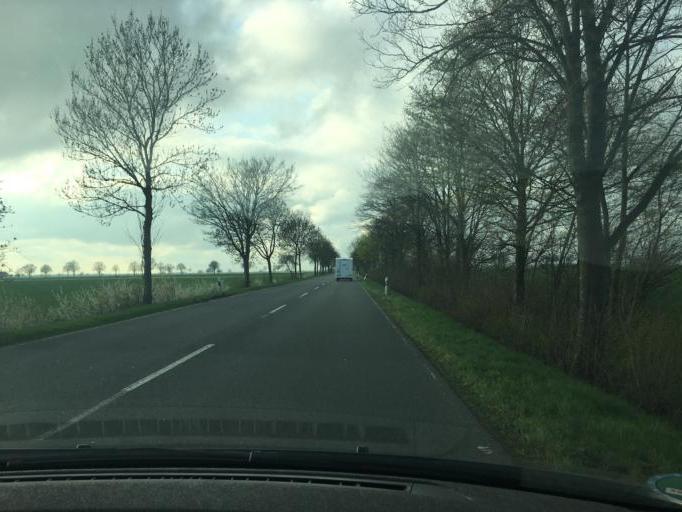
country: DE
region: North Rhine-Westphalia
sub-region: Regierungsbezirk Koln
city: Vettweiss
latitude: 50.7485
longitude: 6.6223
